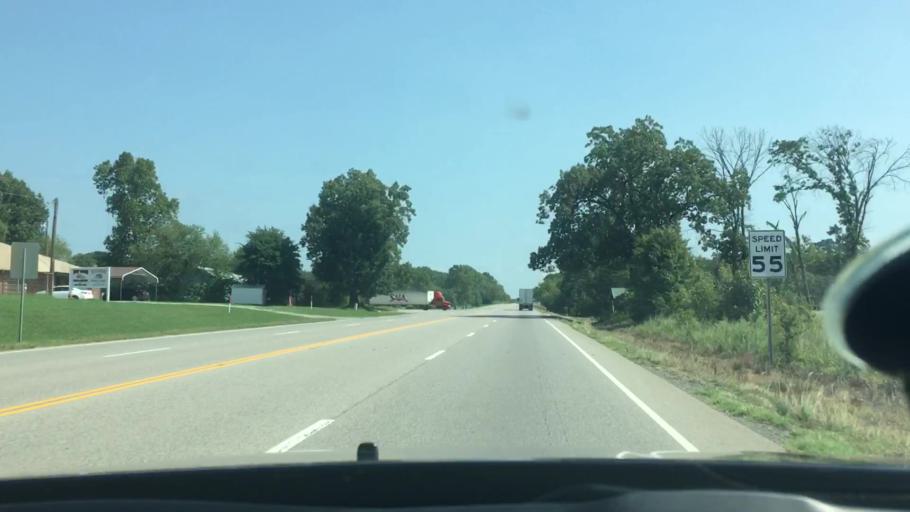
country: US
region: Oklahoma
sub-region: Atoka County
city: Atoka
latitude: 34.3333
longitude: -96.1592
